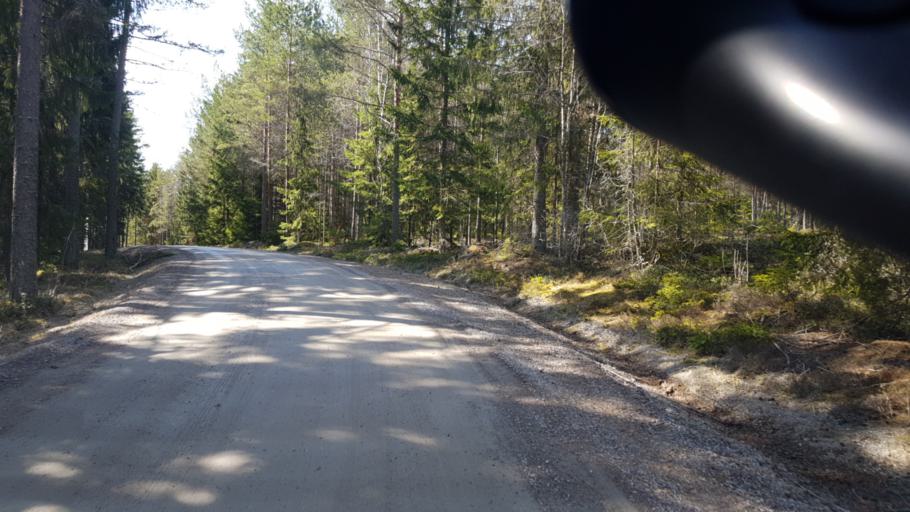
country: SE
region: Vaermland
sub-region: Arvika Kommun
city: Arvika
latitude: 59.5331
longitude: 12.8490
